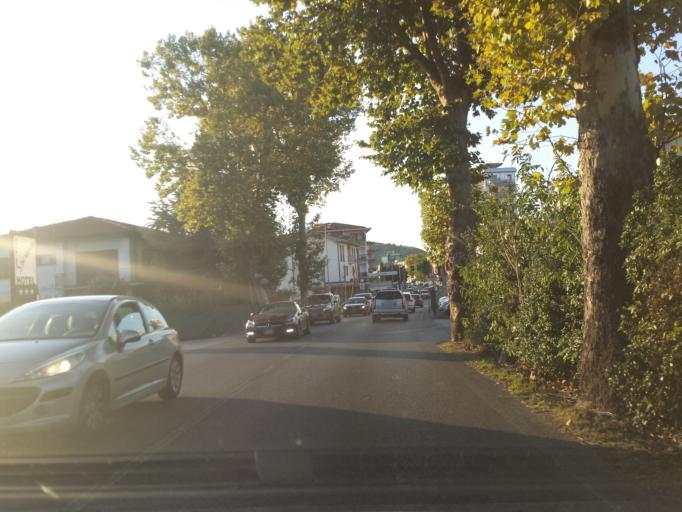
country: IT
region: Veneto
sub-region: Provincia di Vicenza
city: Brendola
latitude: 45.4917
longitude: 11.4348
